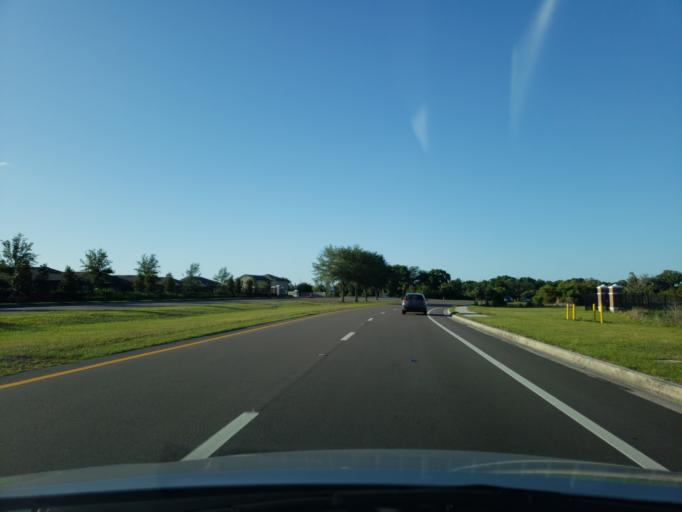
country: US
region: Florida
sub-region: Hillsborough County
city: Progress Village
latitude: 27.8900
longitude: -82.3588
